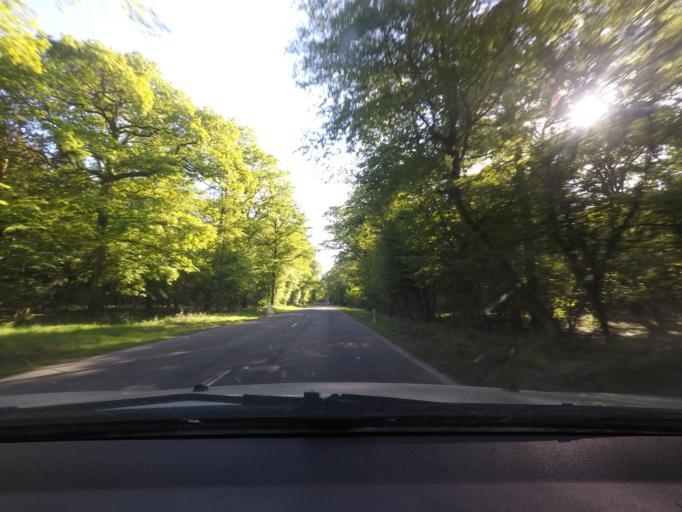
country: BE
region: Wallonia
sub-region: Province de Namur
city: Rochefort
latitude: 50.2004
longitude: 5.1354
